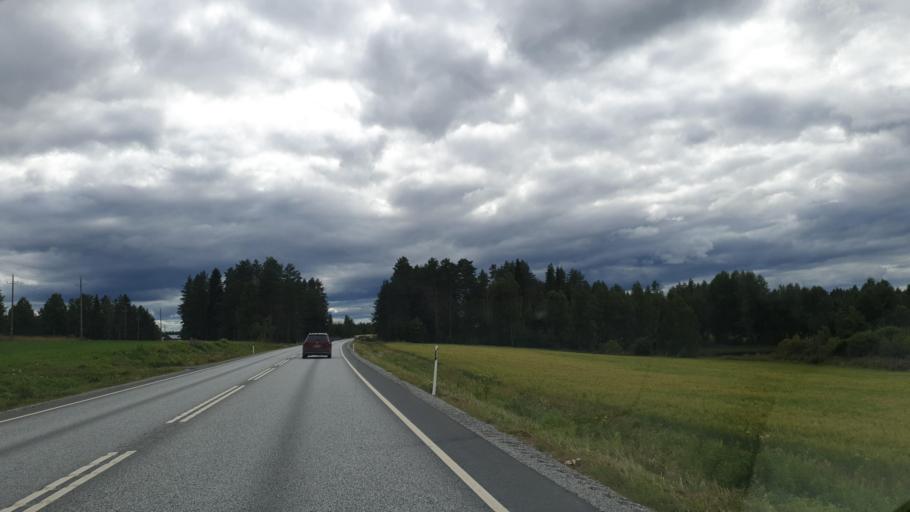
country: FI
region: Northern Savo
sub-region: Ylae-Savo
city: Sonkajaervi
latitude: 63.8450
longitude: 27.4365
